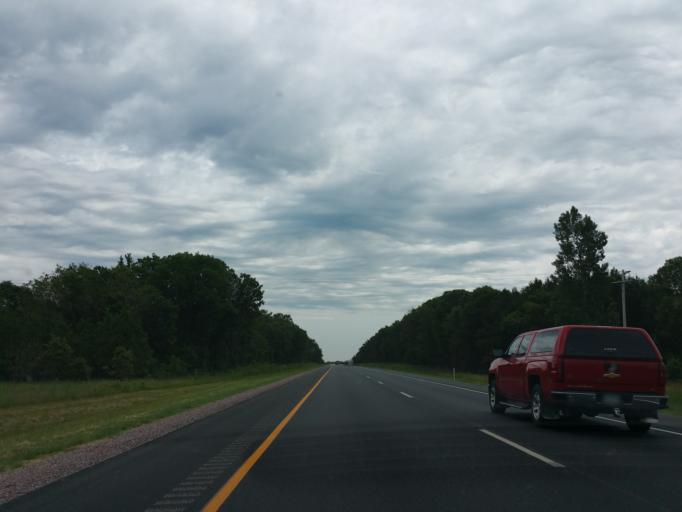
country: US
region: Wisconsin
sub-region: Juneau County
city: Mauston
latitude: 43.7525
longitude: -89.9559
